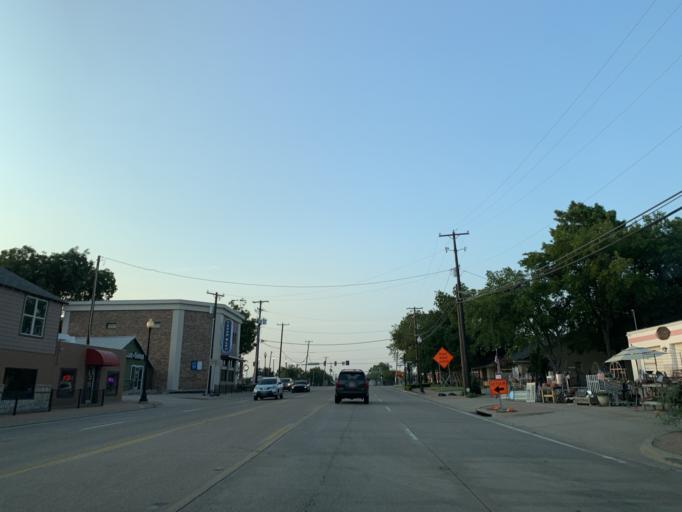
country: US
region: Texas
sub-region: Tarrant County
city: Keller
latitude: 32.9330
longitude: -97.2537
